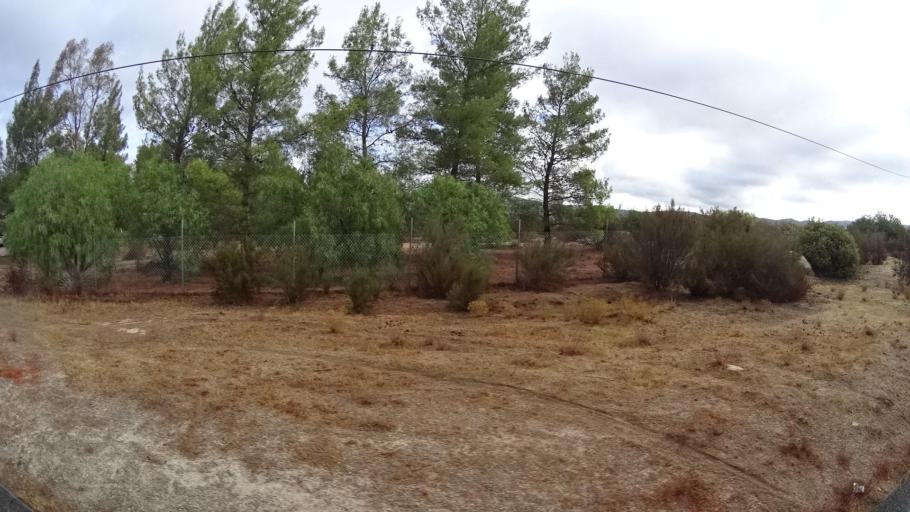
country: MX
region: Baja California
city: Tecate
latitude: 32.6305
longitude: -116.5879
